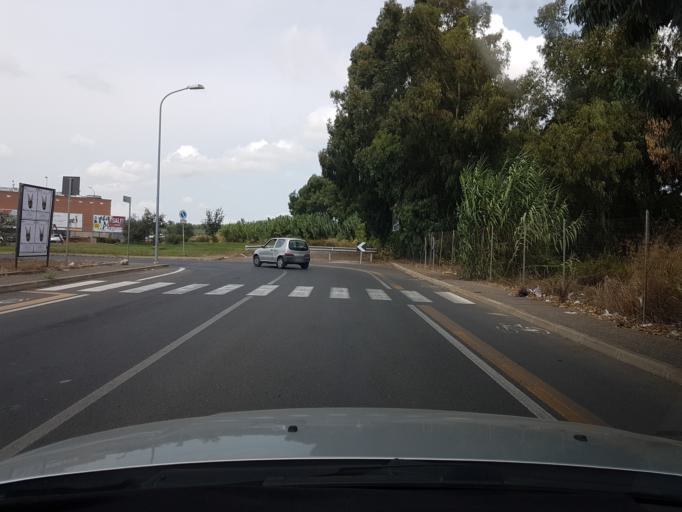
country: IT
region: Sardinia
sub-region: Provincia di Oristano
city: Oristano
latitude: 39.9152
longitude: 8.5884
